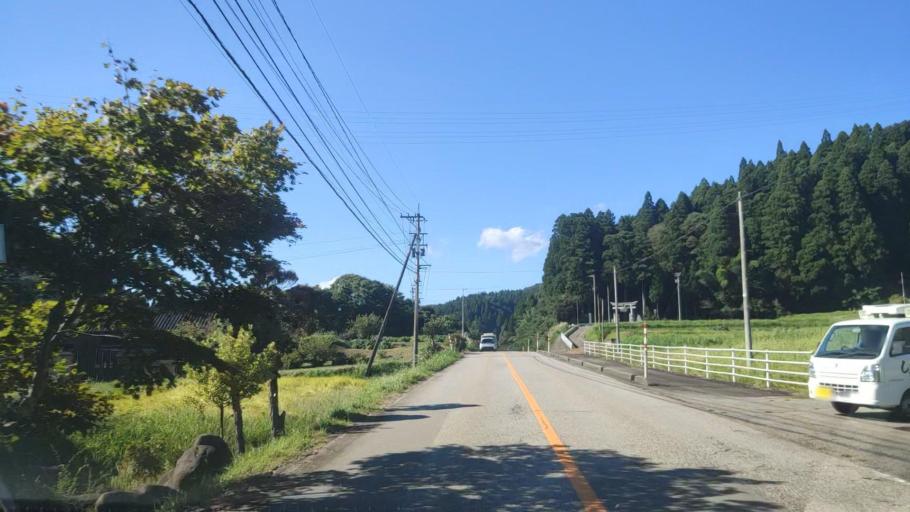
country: JP
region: Ishikawa
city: Nanao
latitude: 37.2734
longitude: 137.0551
